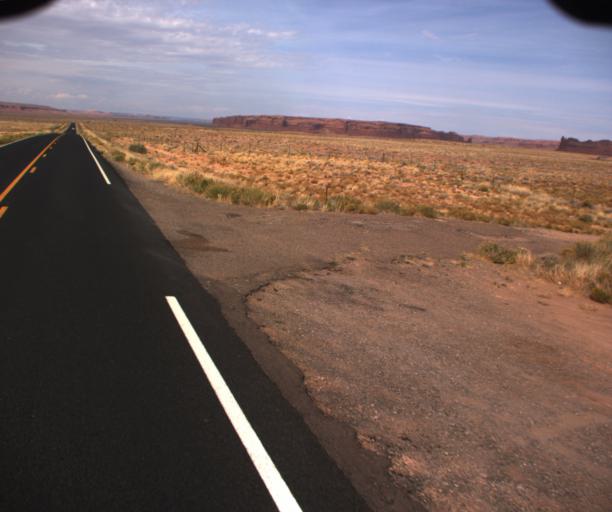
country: US
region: Arizona
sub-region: Apache County
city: Many Farms
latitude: 36.5519
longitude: -109.5320
